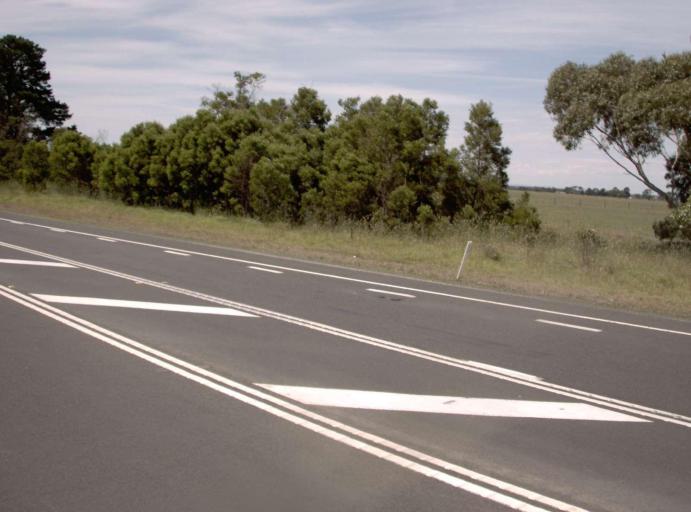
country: AU
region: Victoria
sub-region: Wellington
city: Sale
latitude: -38.0664
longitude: 147.0732
